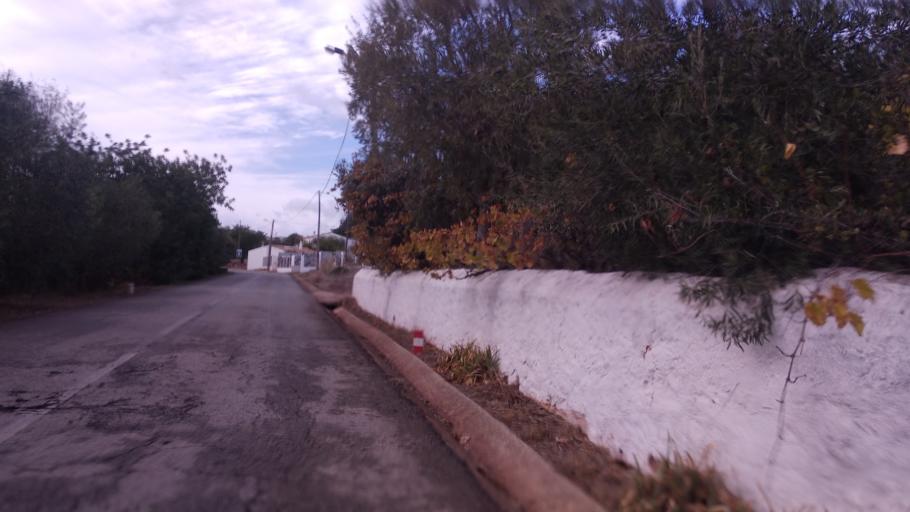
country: PT
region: Faro
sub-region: Sao Bras de Alportel
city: Sao Bras de Alportel
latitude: 37.1751
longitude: -7.8997
